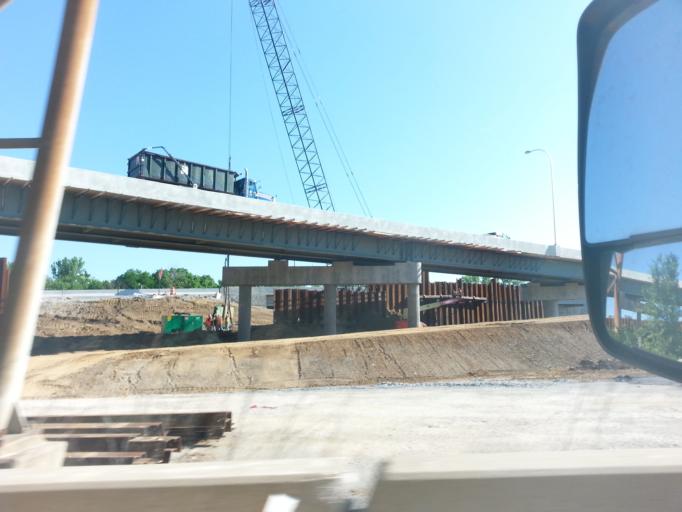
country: US
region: Indiana
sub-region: Clark County
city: Jeffersonville
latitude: 38.2610
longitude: -85.7273
